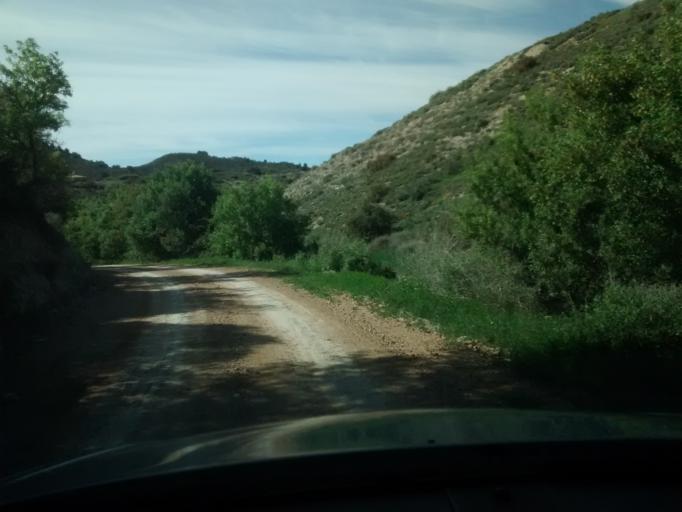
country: ES
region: Aragon
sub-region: Provincia de Huesca
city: Alcubierre
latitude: 41.8165
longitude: -0.5099
